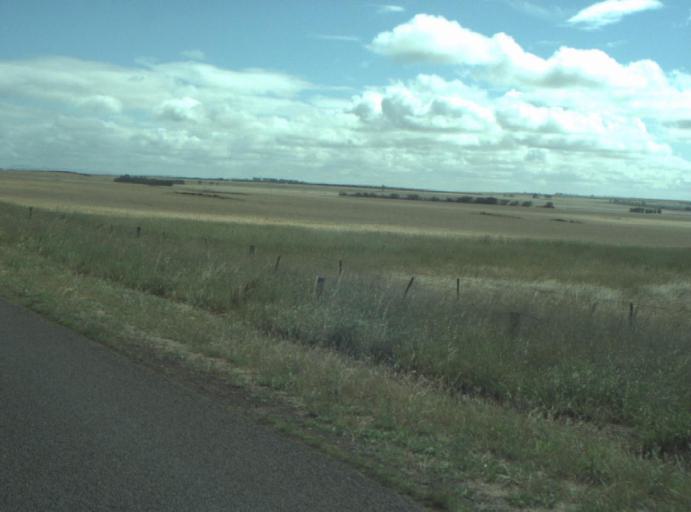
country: AU
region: Victoria
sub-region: Greater Geelong
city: Lara
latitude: -37.9209
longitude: 144.3136
